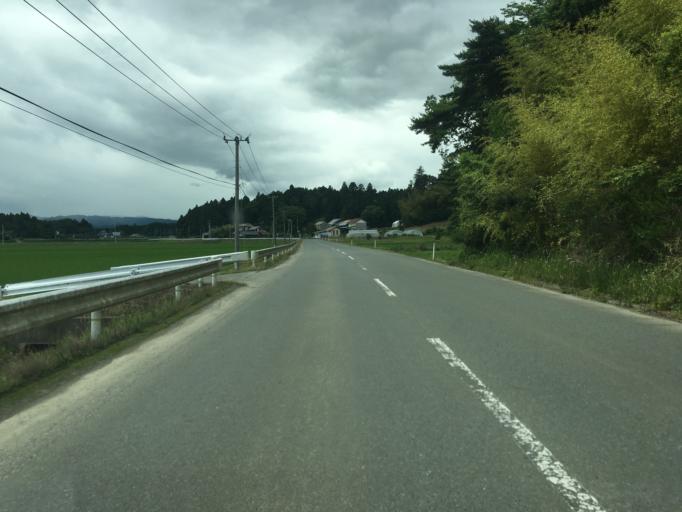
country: JP
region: Fukushima
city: Namie
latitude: 37.7405
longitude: 140.9871
